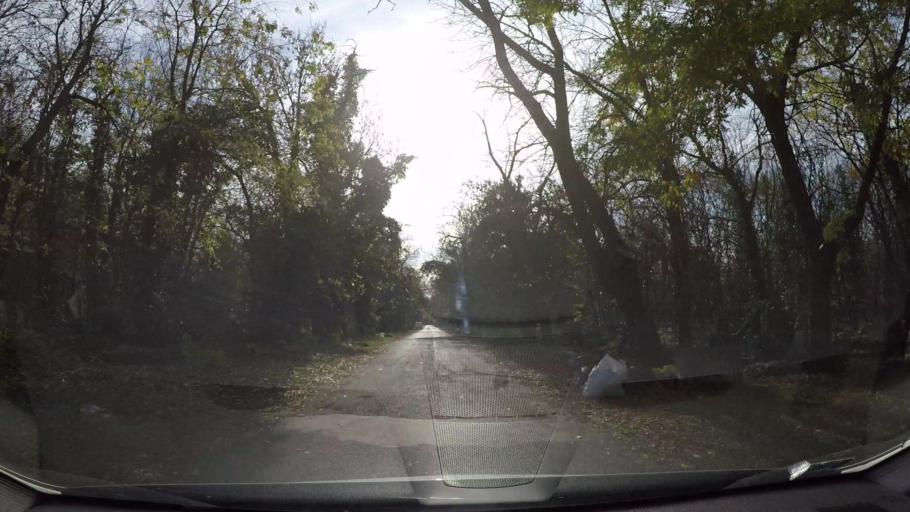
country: HU
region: Budapest
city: Budapest XVIII. keruelet
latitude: 47.4677
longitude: 19.1885
